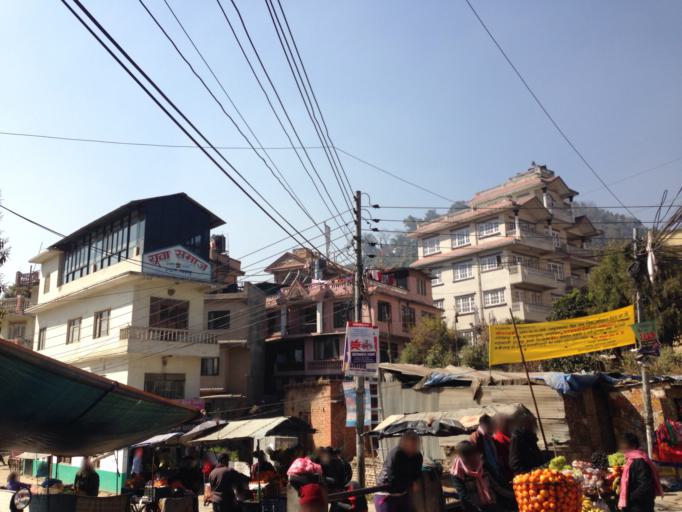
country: NP
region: Central Region
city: Kirtipur
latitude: 27.7167
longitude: 85.2830
